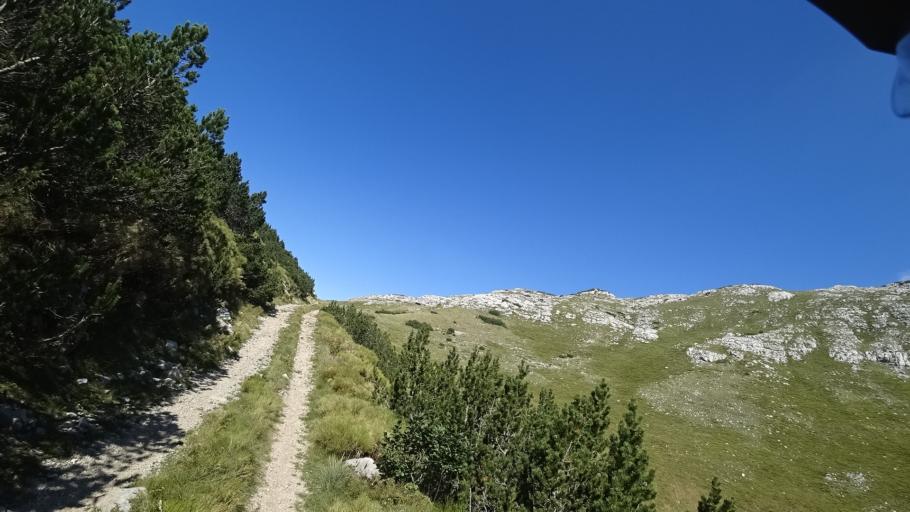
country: HR
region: Splitsko-Dalmatinska
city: Hrvace
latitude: 43.9394
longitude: 16.5863
